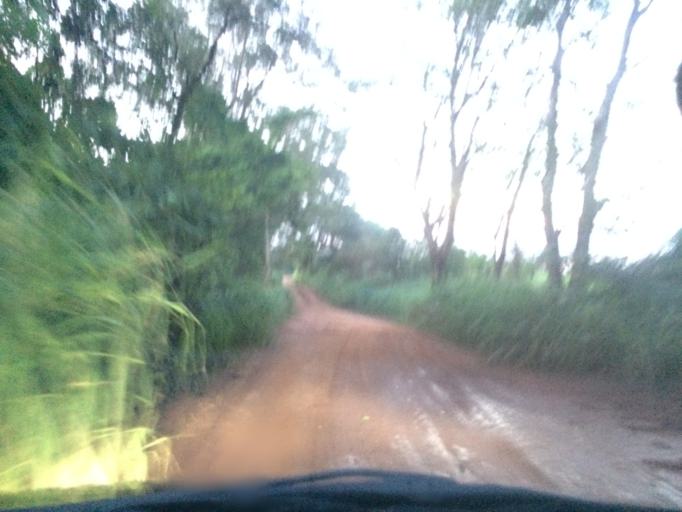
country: BR
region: Sao Paulo
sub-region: Tambau
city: Tambau
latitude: -21.7046
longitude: -47.2270
